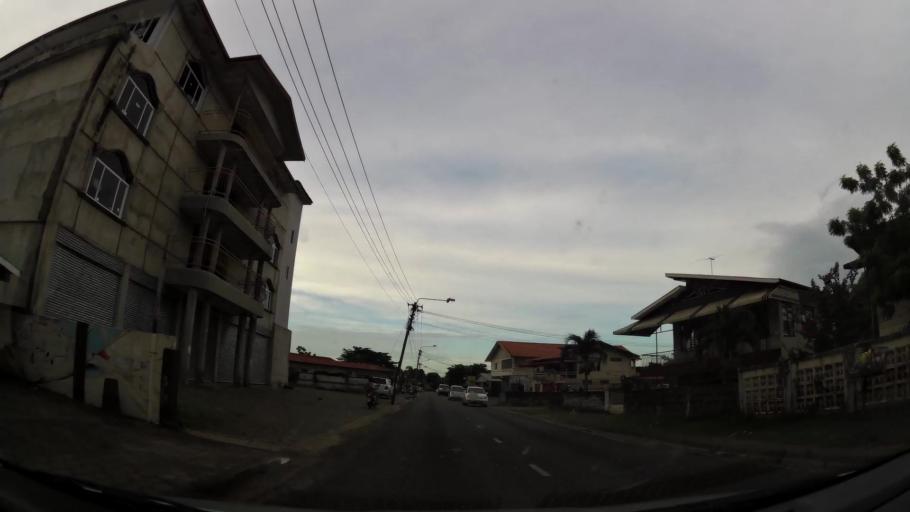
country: SR
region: Paramaribo
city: Paramaribo
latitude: 5.8275
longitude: -55.1990
